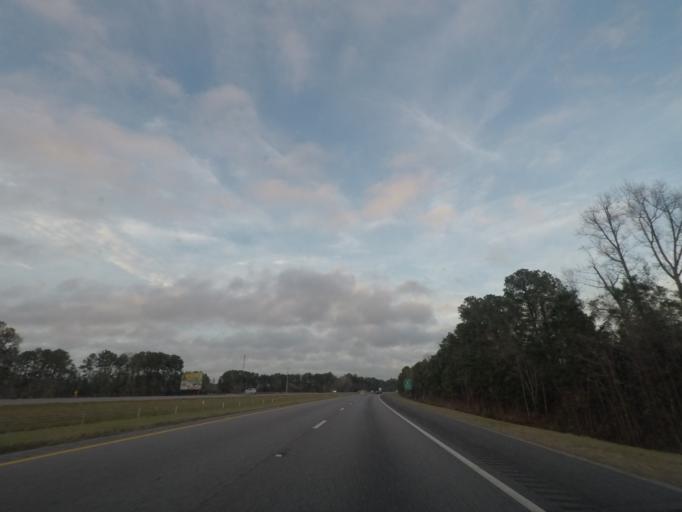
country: US
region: South Carolina
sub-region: Orangeburg County
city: Holly Hill
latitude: 33.3956
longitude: -80.5136
